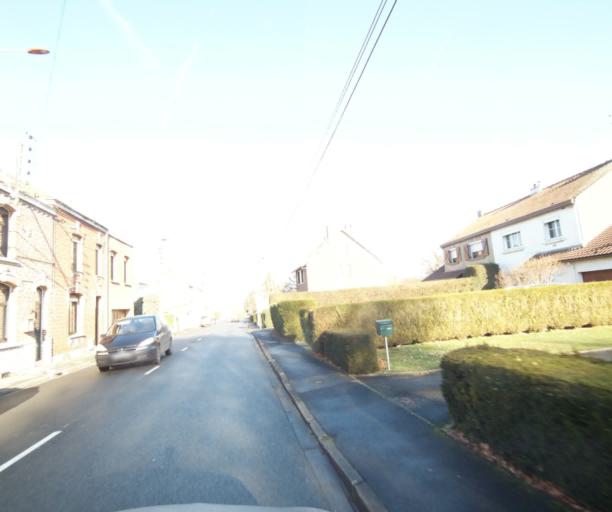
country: FR
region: Nord-Pas-de-Calais
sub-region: Departement du Nord
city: Aulnoy-lez-Valenciennes
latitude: 50.3407
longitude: 3.5294
